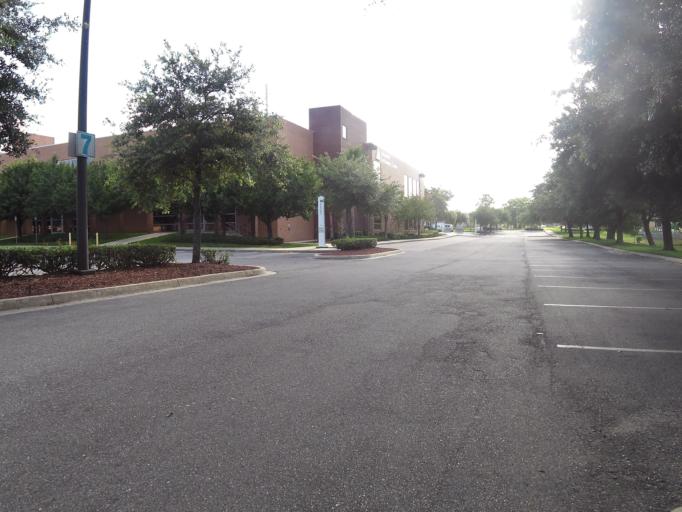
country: US
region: Florida
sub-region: Duval County
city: Jacksonville
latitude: 30.3363
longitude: -81.6607
